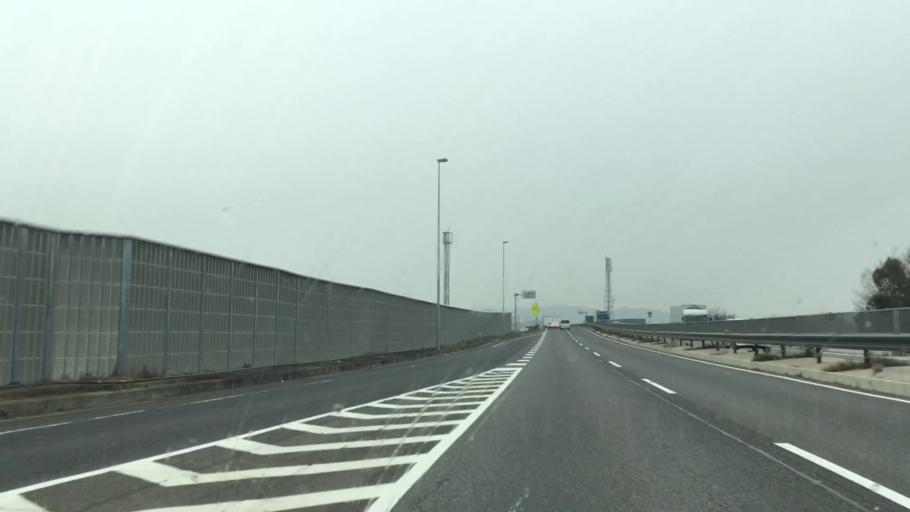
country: JP
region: Aichi
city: Nishio
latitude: 34.8750
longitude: 137.0820
